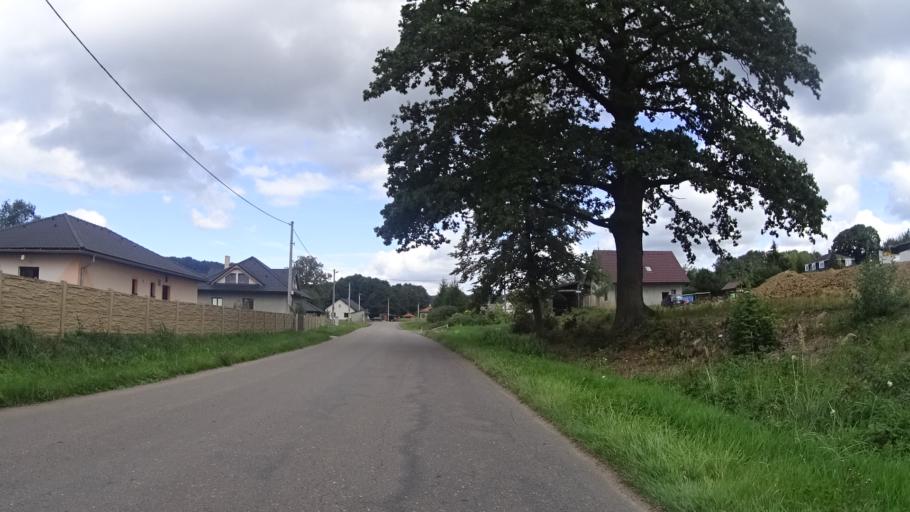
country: CZ
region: Pardubicky
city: Dolni Cermna
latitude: 49.9363
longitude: 16.5312
